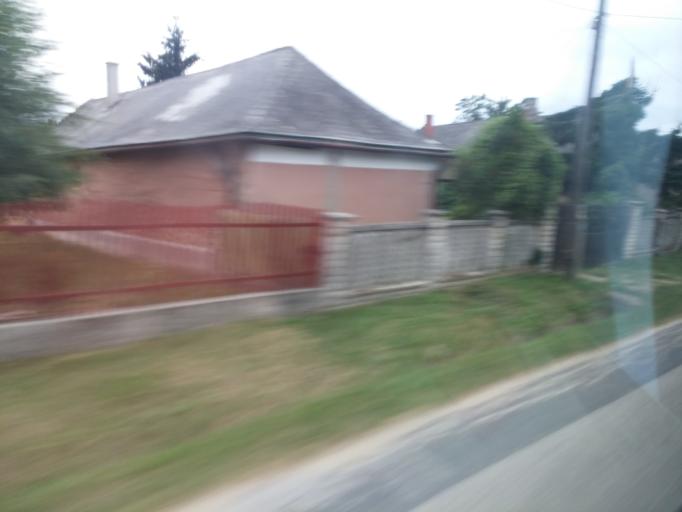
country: HU
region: Fejer
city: Bakonycsernye
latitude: 47.2672
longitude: 18.0476
